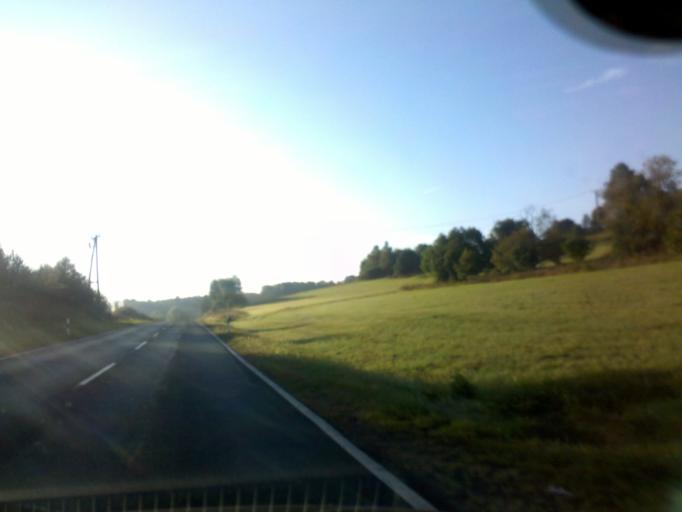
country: DE
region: Hesse
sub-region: Regierungsbezirk Giessen
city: Haiger
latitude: 50.7598
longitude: 8.1968
